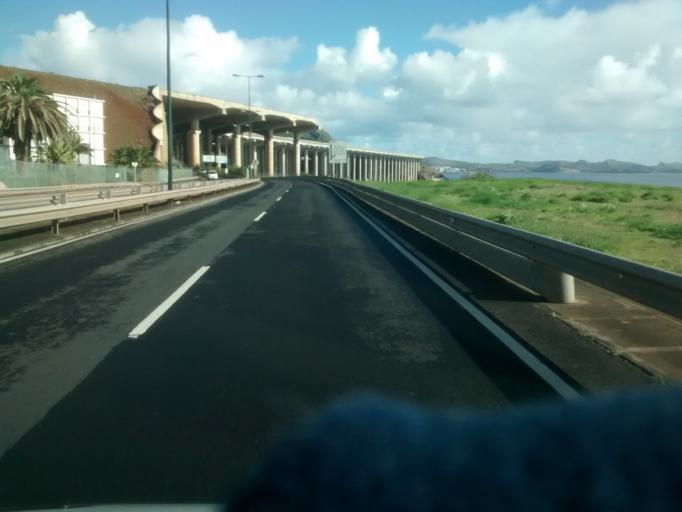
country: PT
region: Madeira
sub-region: Machico
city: Machico
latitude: 32.6964
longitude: -16.7719
